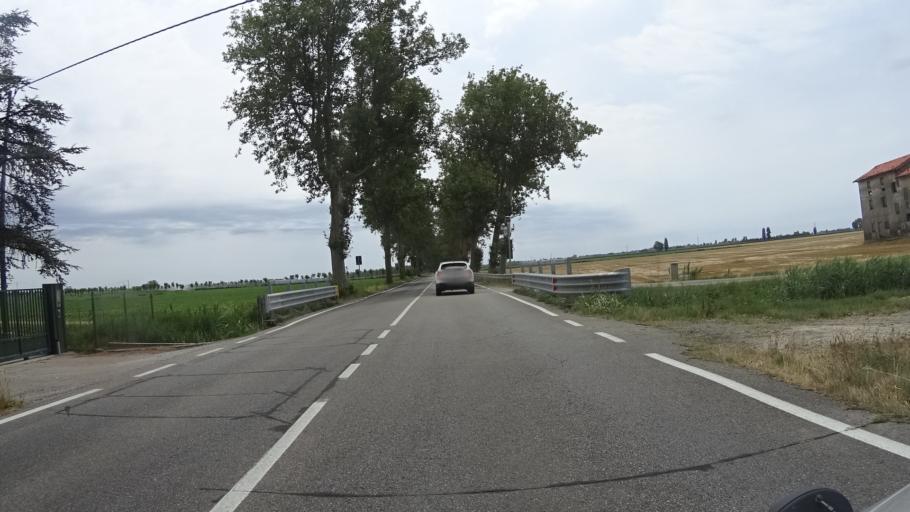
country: IT
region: Veneto
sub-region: Provincia di Venezia
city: San Giorgio di Livenza
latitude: 45.6883
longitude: 12.7754
